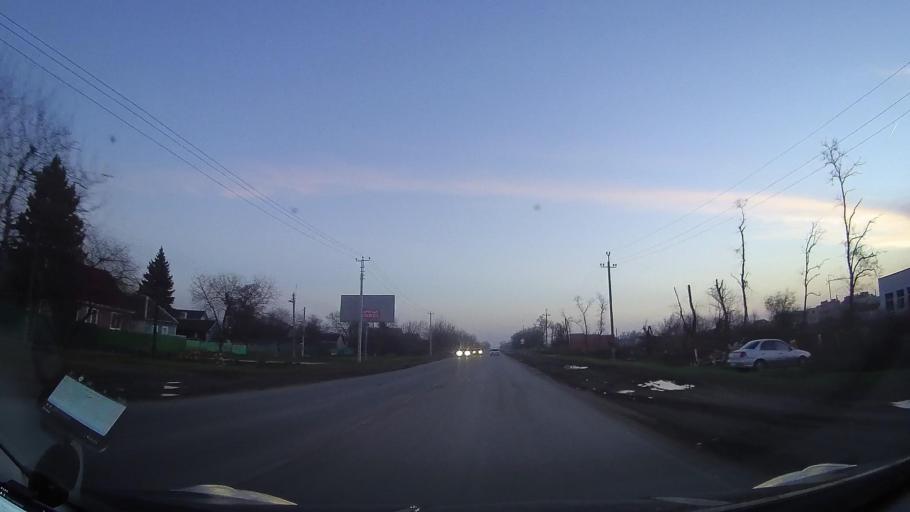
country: RU
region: Rostov
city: Zernograd
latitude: 46.8417
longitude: 40.2994
